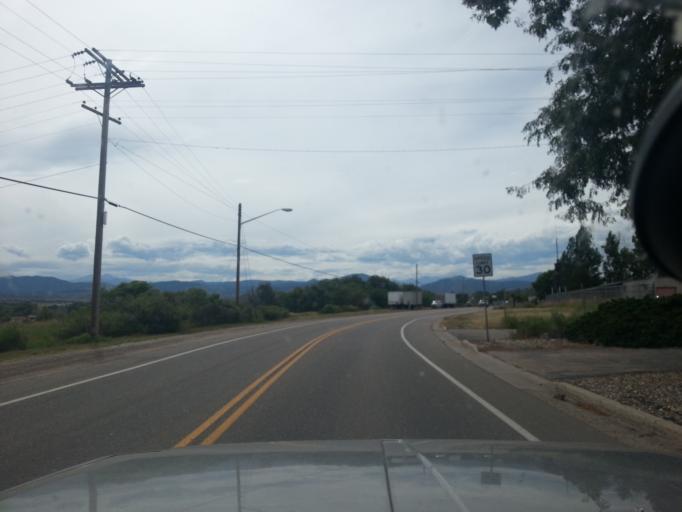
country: US
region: Colorado
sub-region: Larimer County
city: Loveland
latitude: 40.4015
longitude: -105.1059
